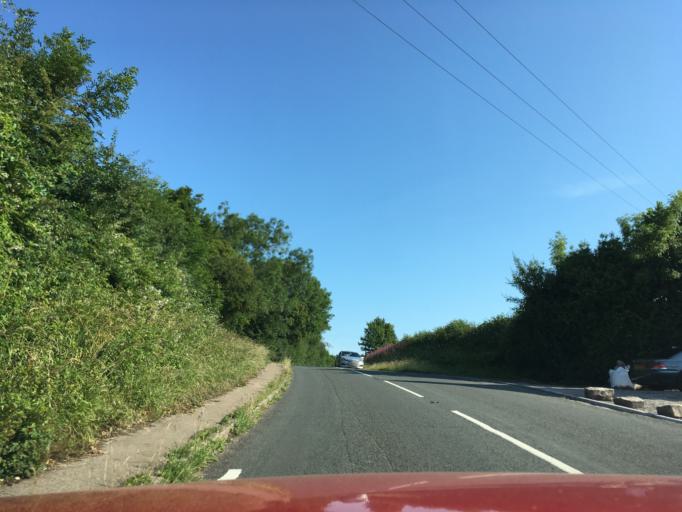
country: GB
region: England
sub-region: Gloucestershire
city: Lydney
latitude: 51.7622
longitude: -2.4821
